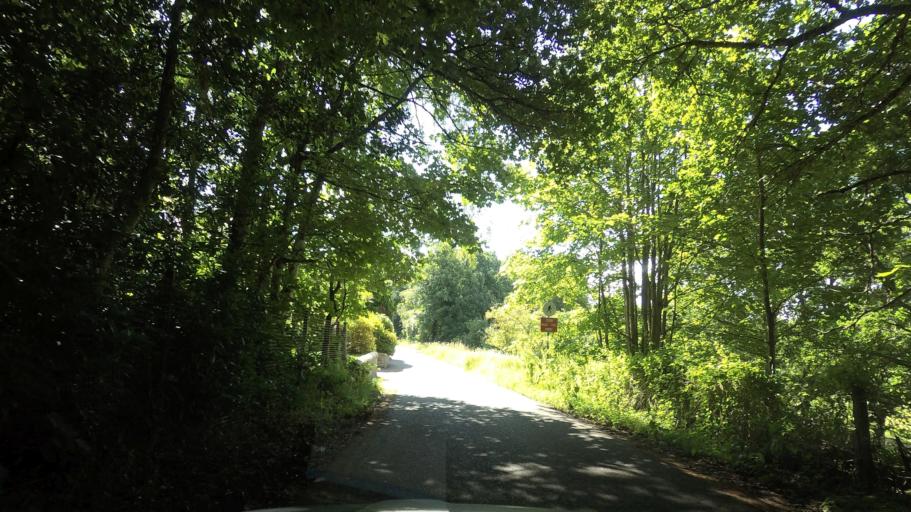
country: GB
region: Scotland
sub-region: Stirling
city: Killearn
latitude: 56.0650
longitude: -4.4747
